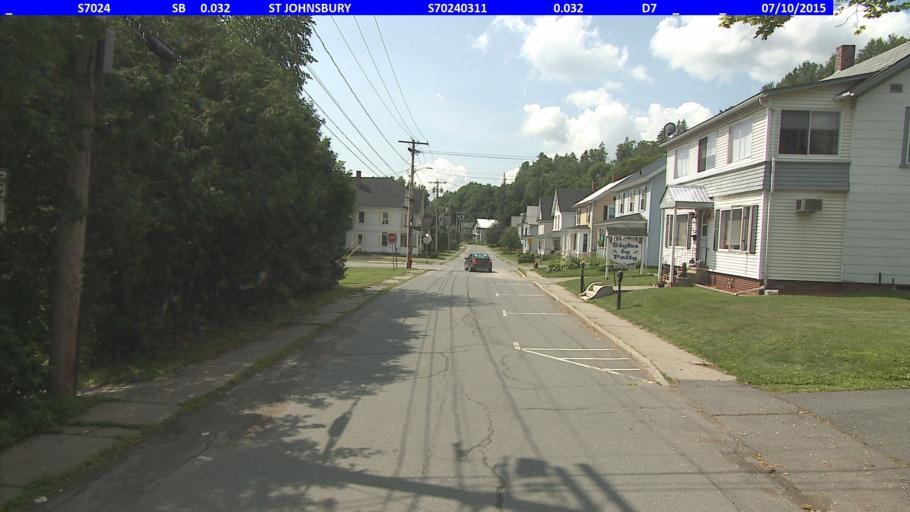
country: US
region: Vermont
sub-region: Caledonia County
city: Saint Johnsbury
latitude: 44.4168
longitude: -72.0173
